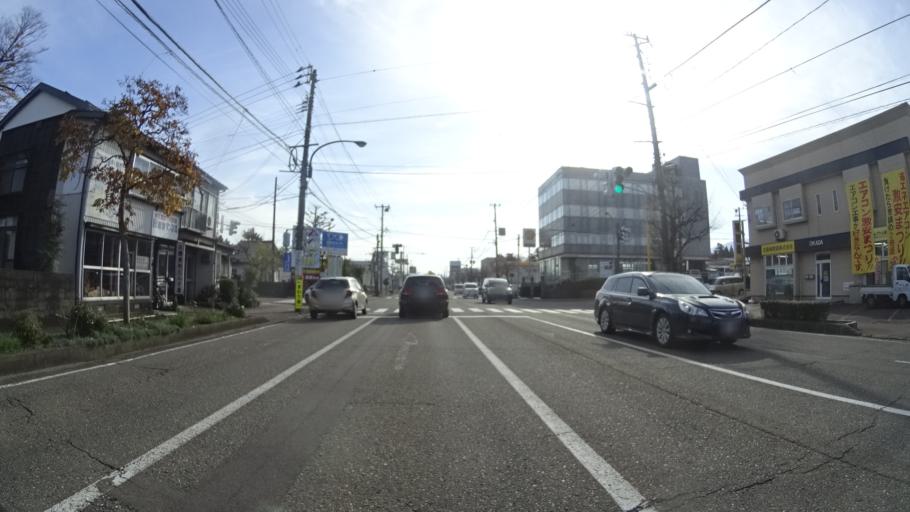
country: JP
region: Niigata
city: Joetsu
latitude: 37.1193
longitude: 138.2520
